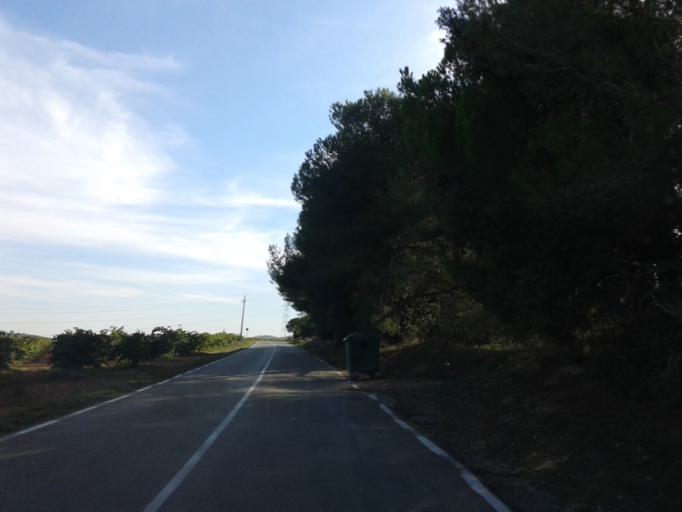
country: ES
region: Catalonia
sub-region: Provincia de Barcelona
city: Vilafranca del Penedes
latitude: 41.3351
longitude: 1.7258
